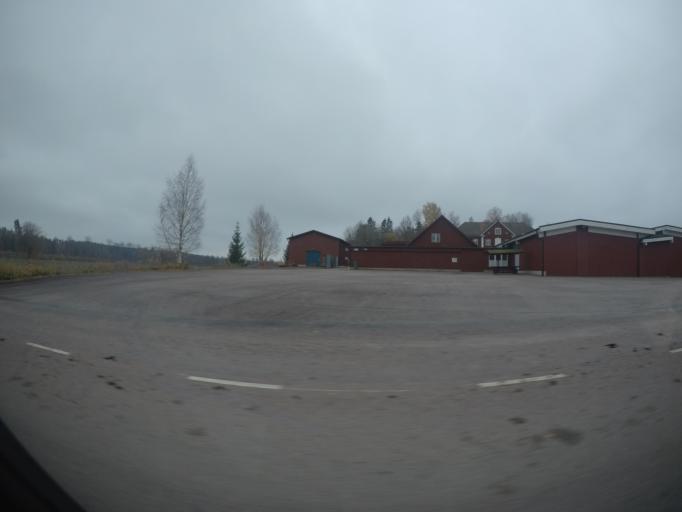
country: SE
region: Vaestmanland
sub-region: Surahammars Kommun
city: Ramnas
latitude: 59.6999
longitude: 16.0701
